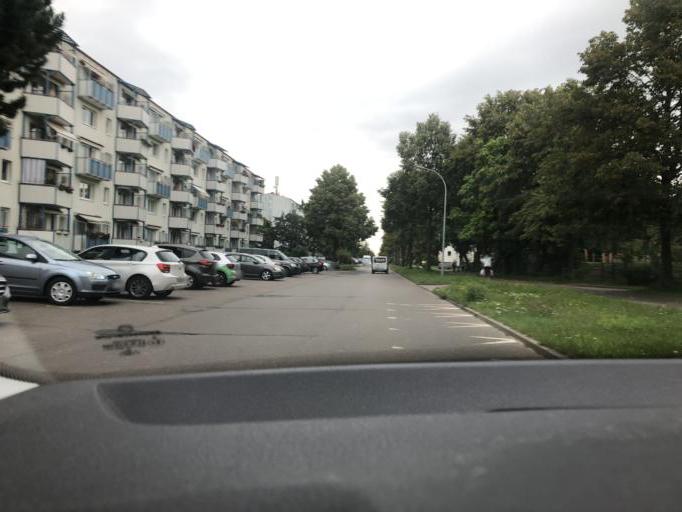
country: DE
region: Mecklenburg-Vorpommern
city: Lankow
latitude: 53.6482
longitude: 11.3664
